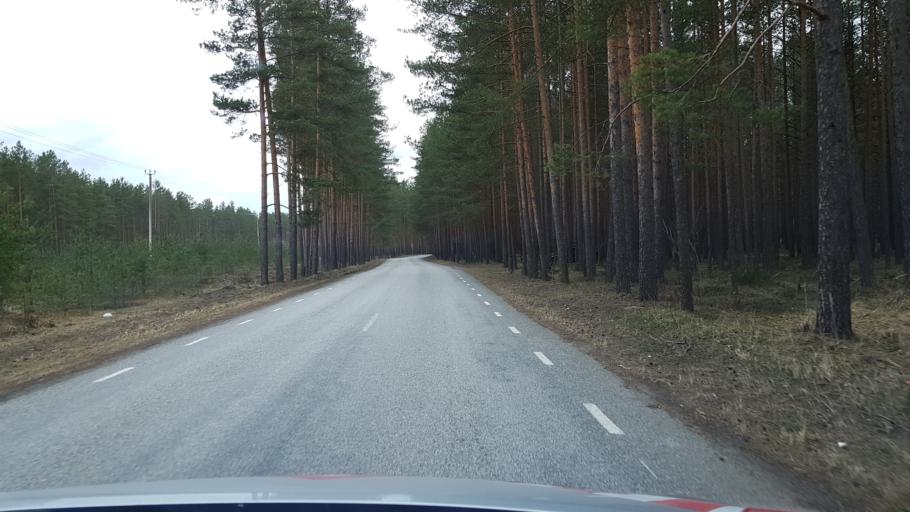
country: EE
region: Ida-Virumaa
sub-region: Narva-Joesuu linn
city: Narva-Joesuu
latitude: 59.4240
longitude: 28.1172
